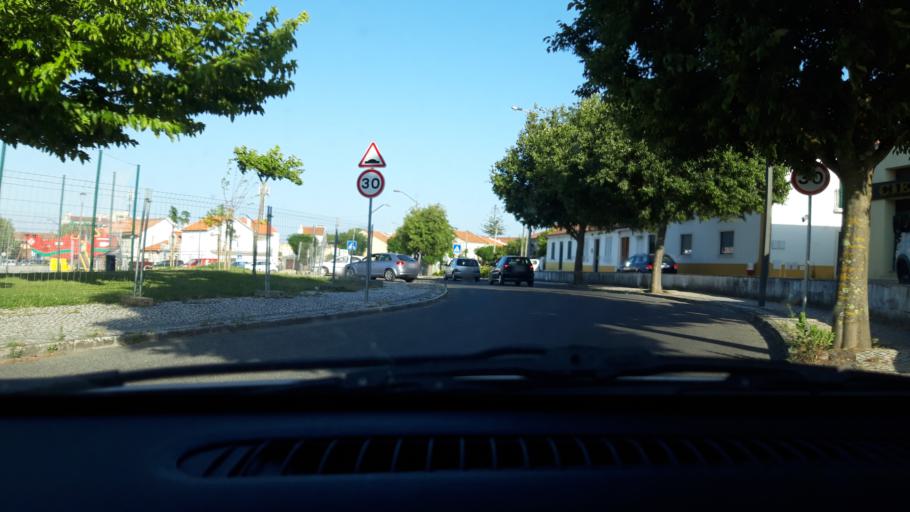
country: PT
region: Santarem
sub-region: Torres Novas
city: Torres Novas
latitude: 39.4776
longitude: -8.5461
